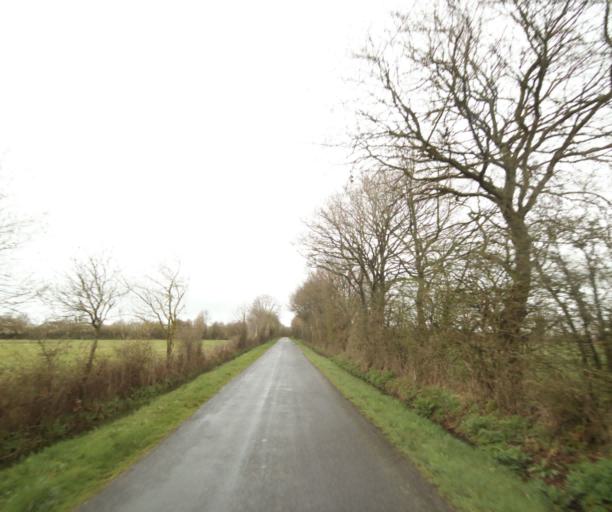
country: FR
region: Pays de la Loire
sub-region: Departement de la Loire-Atlantique
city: Bouvron
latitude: 47.4536
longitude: -1.8784
